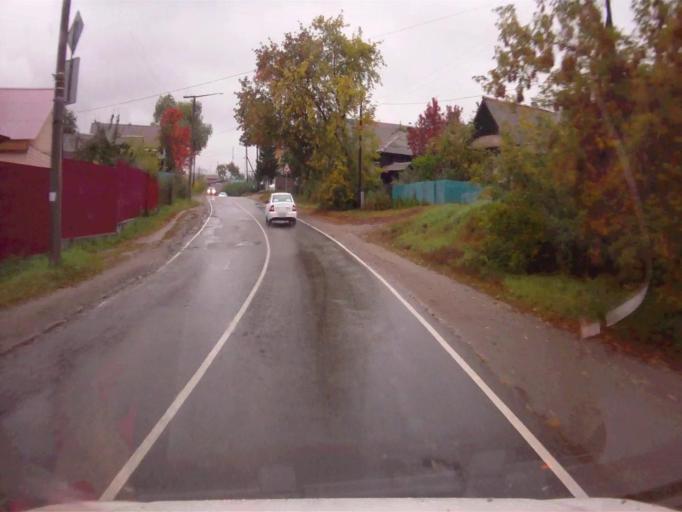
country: RU
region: Chelyabinsk
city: Kyshtym
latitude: 55.7237
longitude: 60.5262
